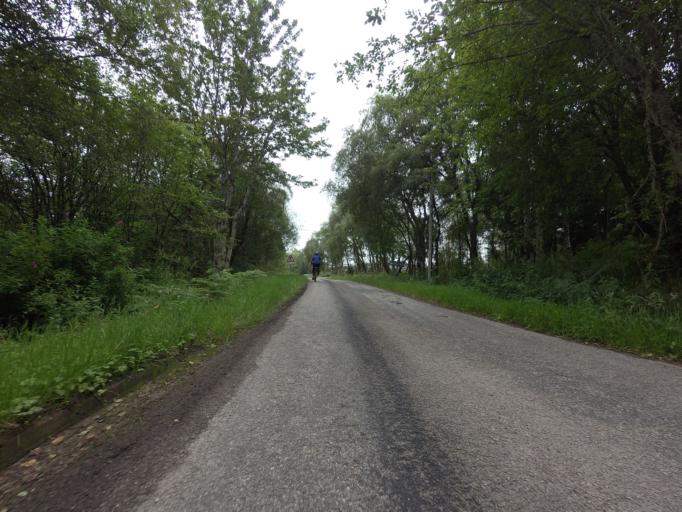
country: GB
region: Scotland
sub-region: Highland
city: Evanton
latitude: 57.9614
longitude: -4.4081
